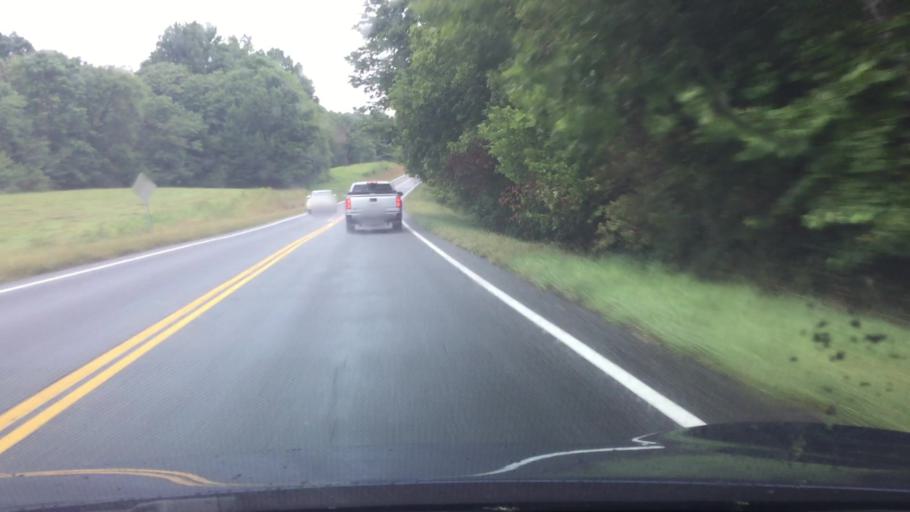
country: US
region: Virginia
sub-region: Bedford County
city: Forest
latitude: 37.3662
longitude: -79.3961
